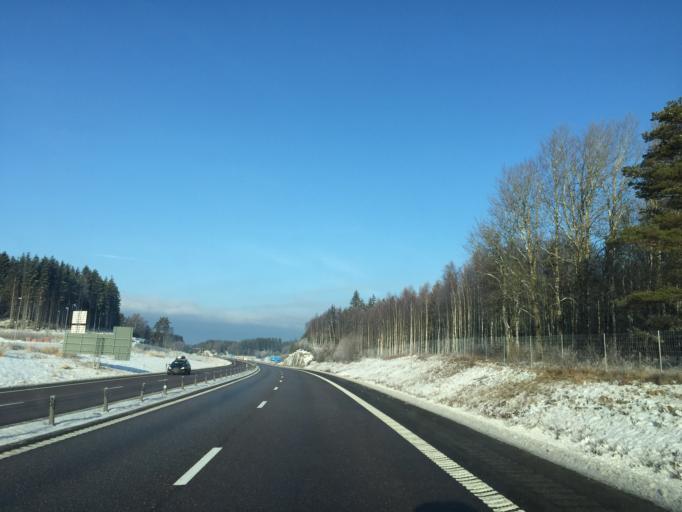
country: SE
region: Vaestra Goetaland
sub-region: Tanums Kommun
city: Tanumshede
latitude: 58.7241
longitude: 11.3501
